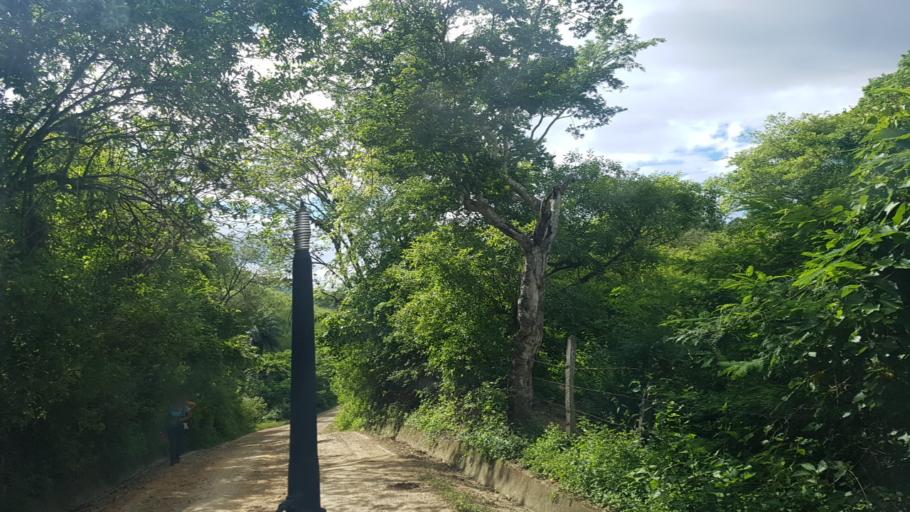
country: HN
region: El Paraiso
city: Oropoli
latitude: 13.7443
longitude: -86.7067
